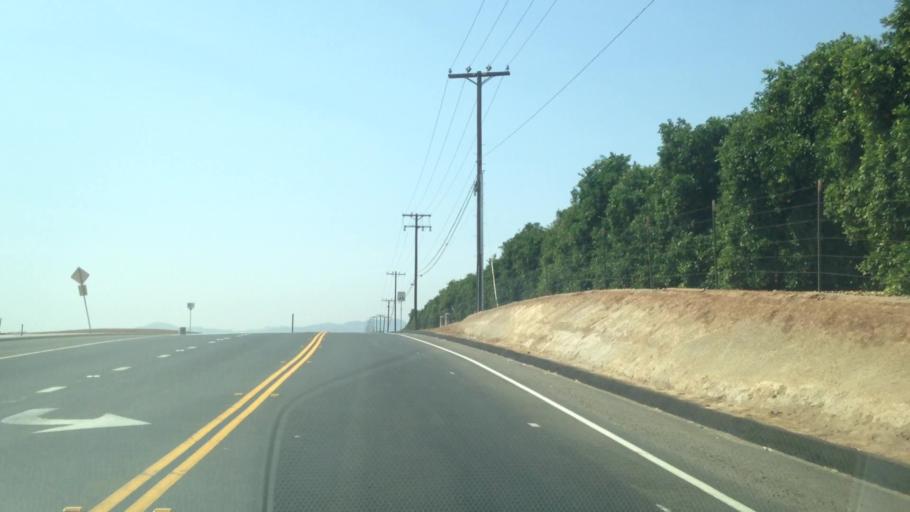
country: US
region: California
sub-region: Riverside County
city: Woodcrest
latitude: 33.8877
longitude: -117.3139
